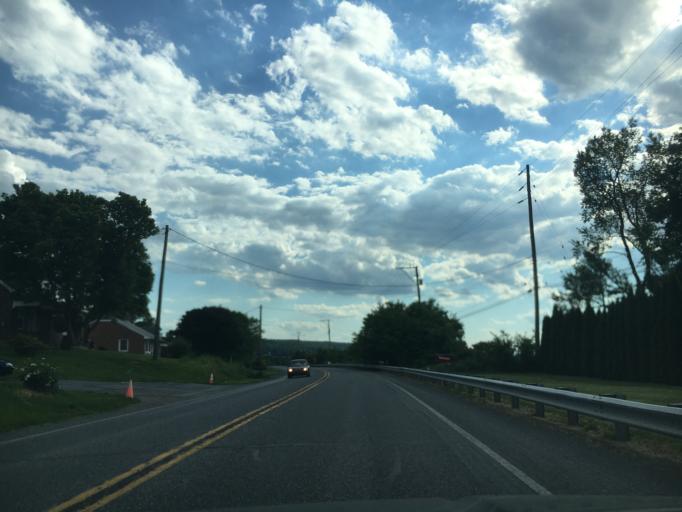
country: US
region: Pennsylvania
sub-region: Berks County
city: Fleetwood
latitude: 40.4678
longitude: -75.8041
